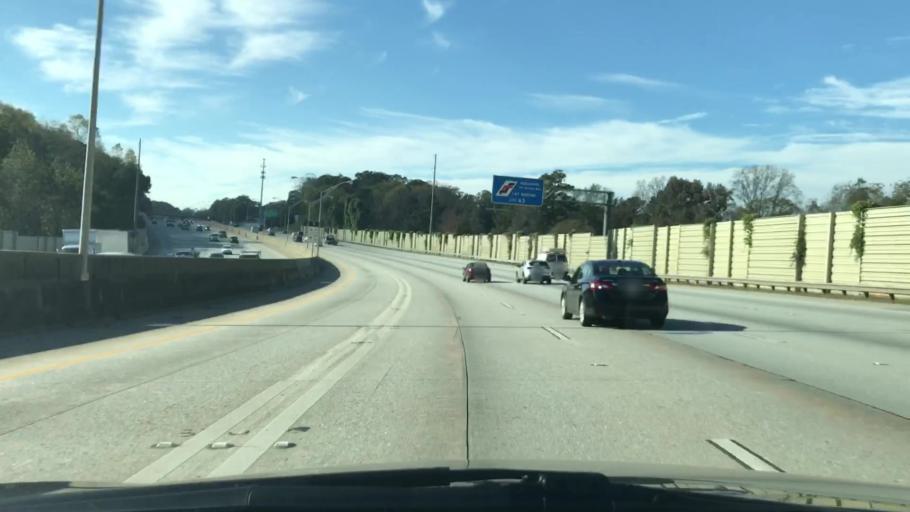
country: US
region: Georgia
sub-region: DeKalb County
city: Gresham Park
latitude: 33.7149
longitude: -84.2973
